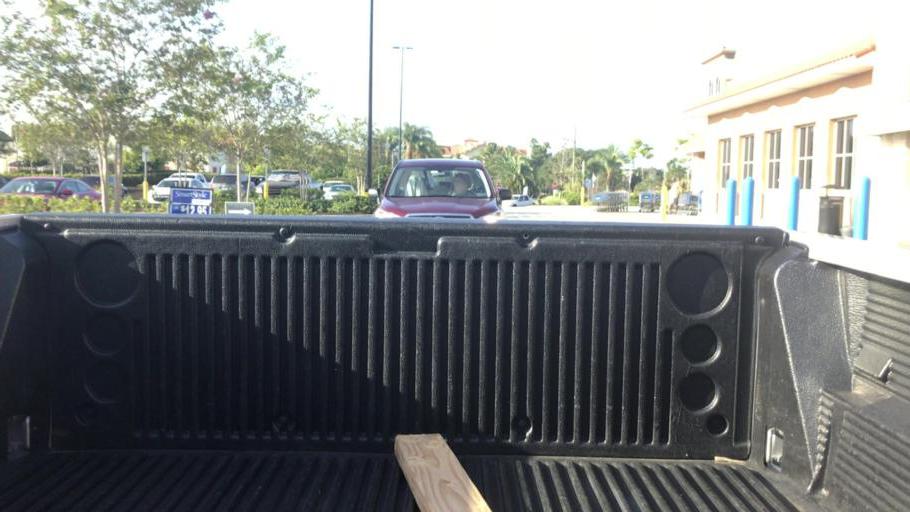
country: US
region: Florida
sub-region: Pinellas County
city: Bay Pines
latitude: 27.8155
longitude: -82.7807
